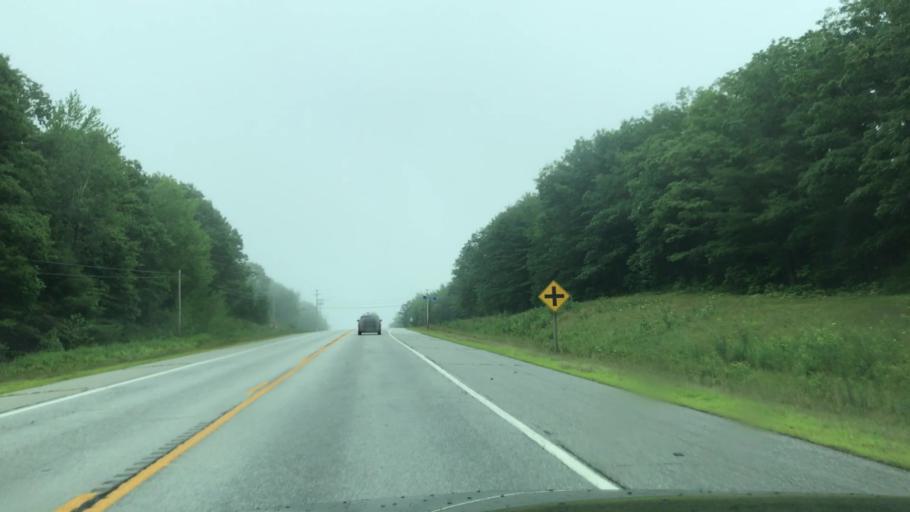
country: US
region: Maine
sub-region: Lincoln County
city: Nobleboro
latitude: 44.0699
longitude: -69.4847
